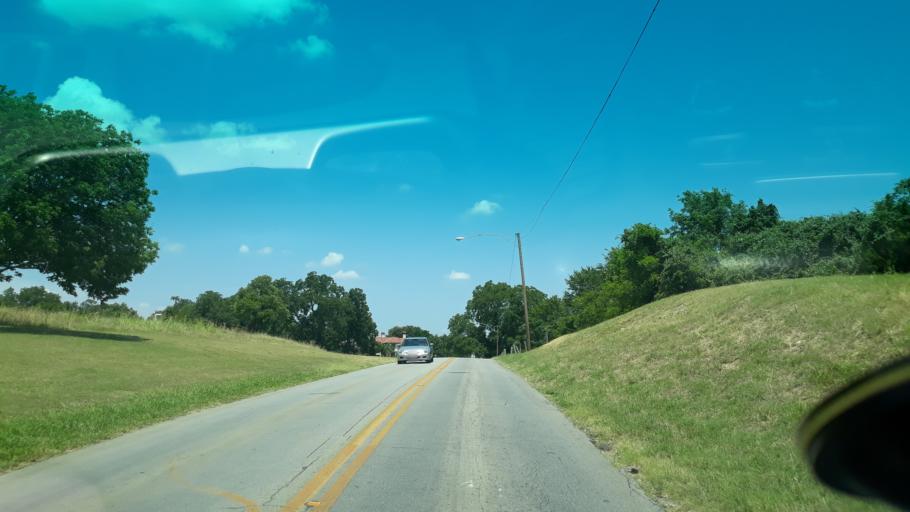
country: US
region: Texas
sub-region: Dallas County
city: Highland Park
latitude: 32.8211
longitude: -96.7312
